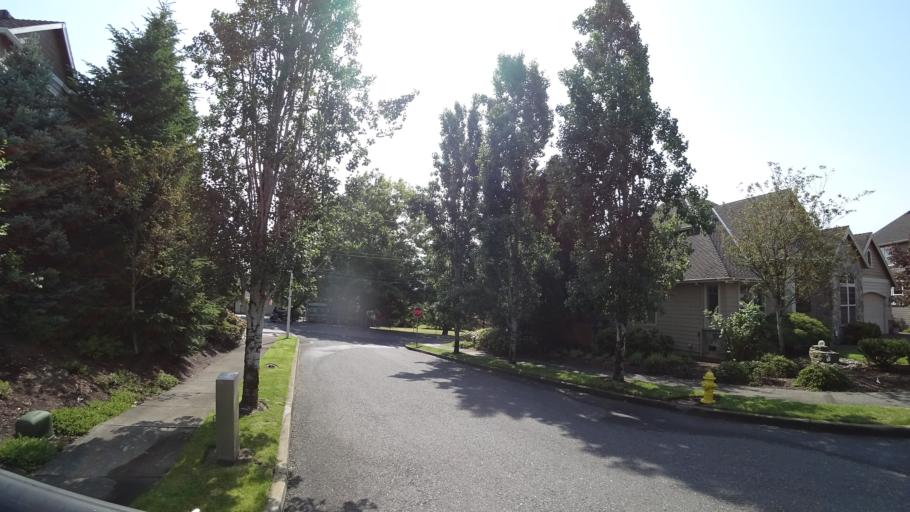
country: US
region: Oregon
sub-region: Clackamas County
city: Happy Valley
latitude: 45.4602
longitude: -122.5148
